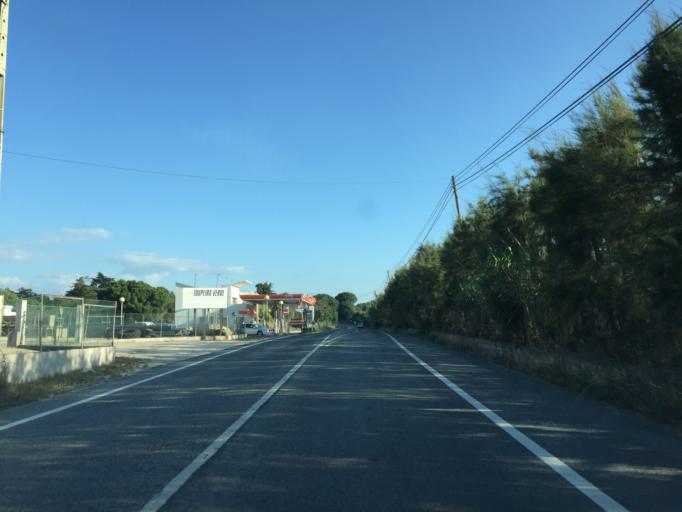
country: PT
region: Lisbon
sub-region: Alenquer
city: Alenquer
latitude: 39.0950
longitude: -8.9923
